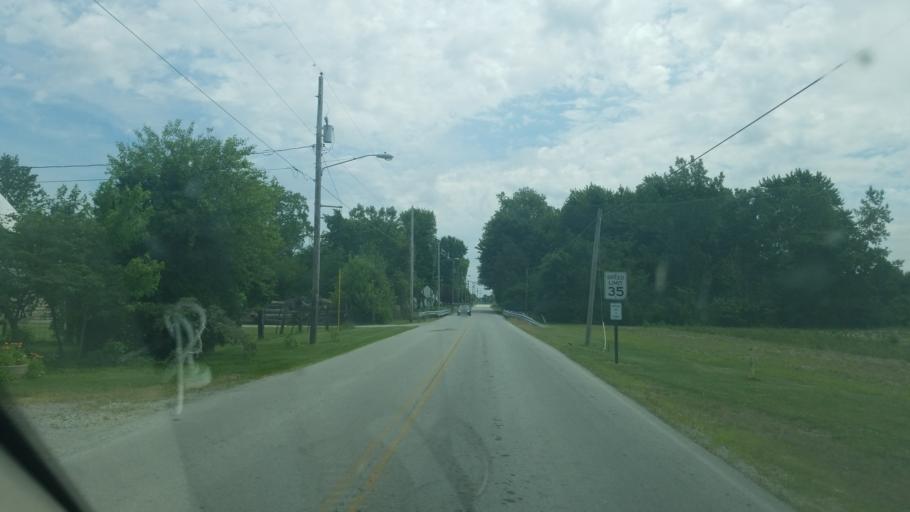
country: US
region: Ohio
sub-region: Wood County
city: Bowling Green
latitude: 41.2975
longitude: -83.6500
